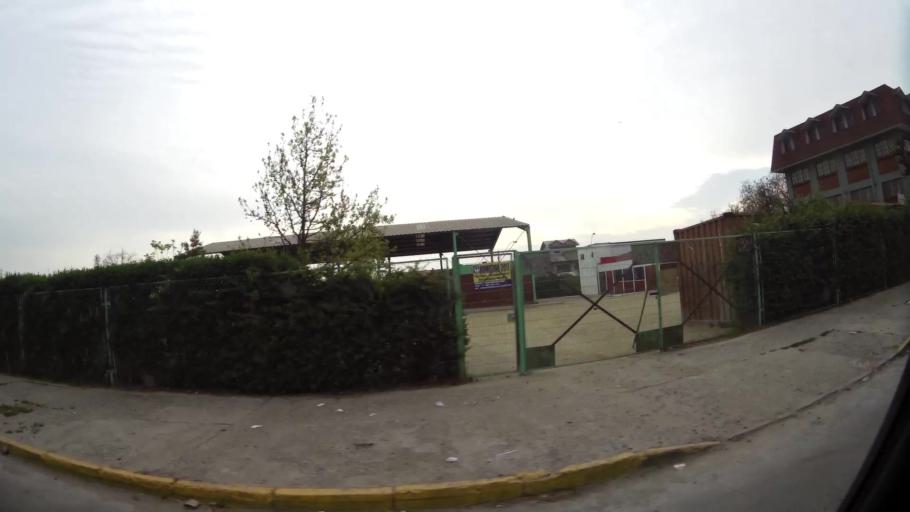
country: CL
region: Santiago Metropolitan
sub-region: Provincia de Santiago
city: Lo Prado
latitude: -33.5123
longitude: -70.7711
